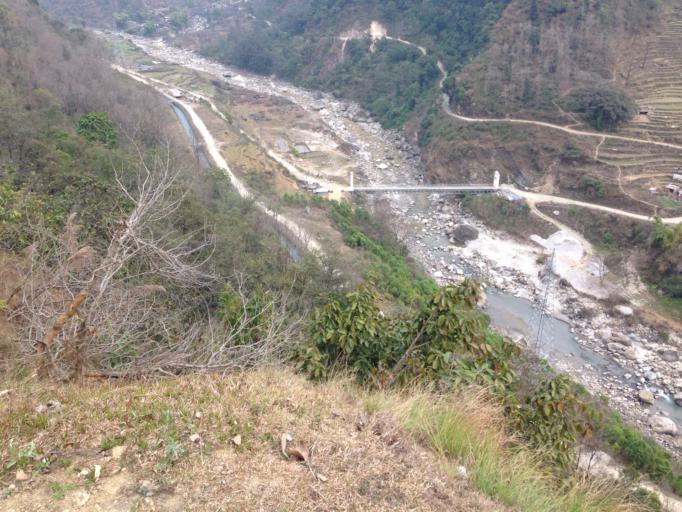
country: NP
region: Western Region
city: Baglung
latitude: 28.2258
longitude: 83.7077
